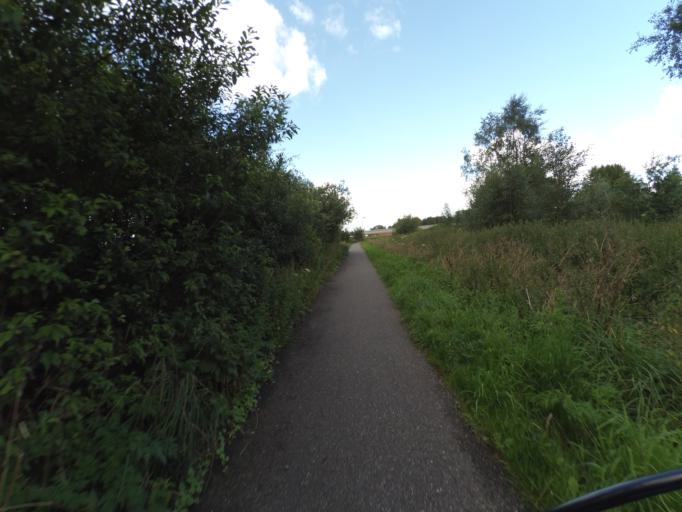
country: NL
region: Friesland
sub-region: Gemeente Dantumadiel
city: De Westereen
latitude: 53.2621
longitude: 6.0156
